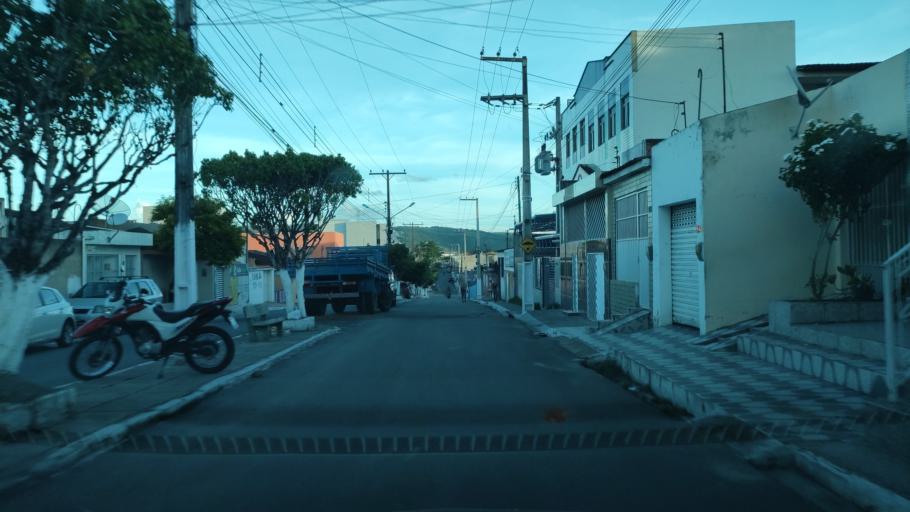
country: BR
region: Alagoas
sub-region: Uniao Dos Palmares
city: Uniao dos Palmares
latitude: -9.1561
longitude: -36.0305
